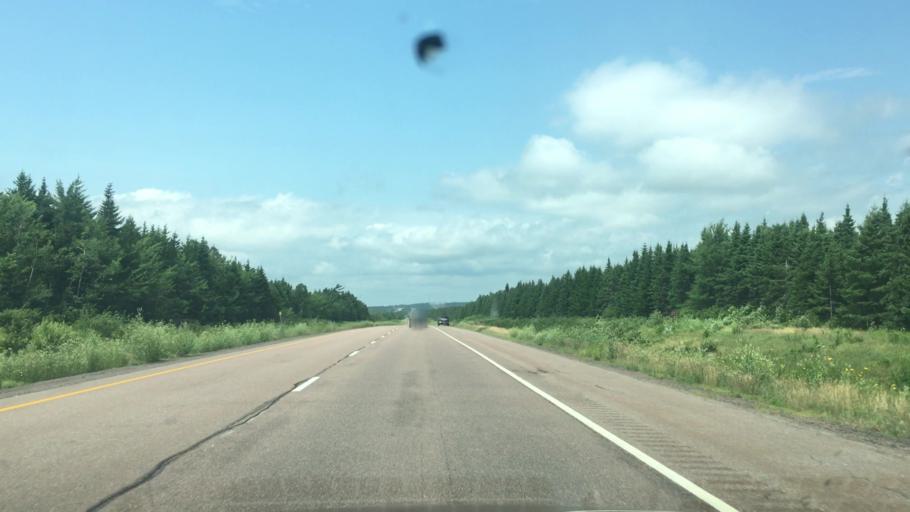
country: CA
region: New Brunswick
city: Sackville
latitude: 45.9707
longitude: -64.4348
